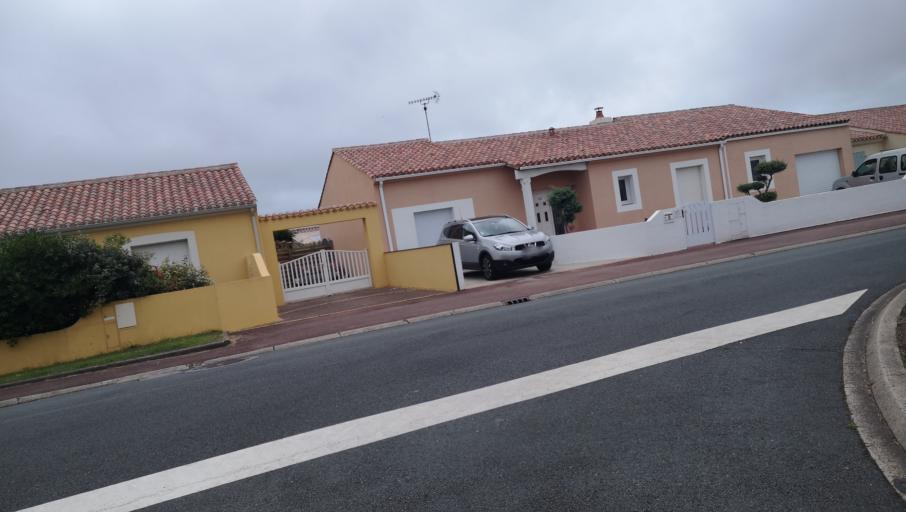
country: FR
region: Pays de la Loire
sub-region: Departement de la Vendee
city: Les Sables-d'Olonne
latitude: 46.5114
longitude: -1.7821
